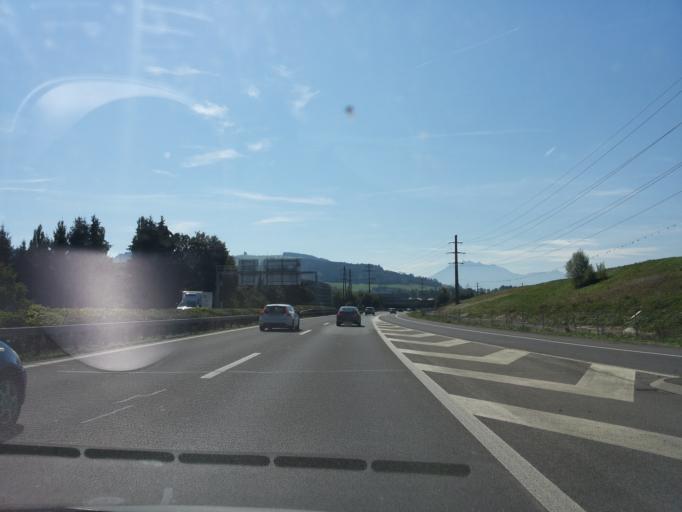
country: CH
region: Zug
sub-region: Zug
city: Hunenberg
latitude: 47.1532
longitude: 8.4313
